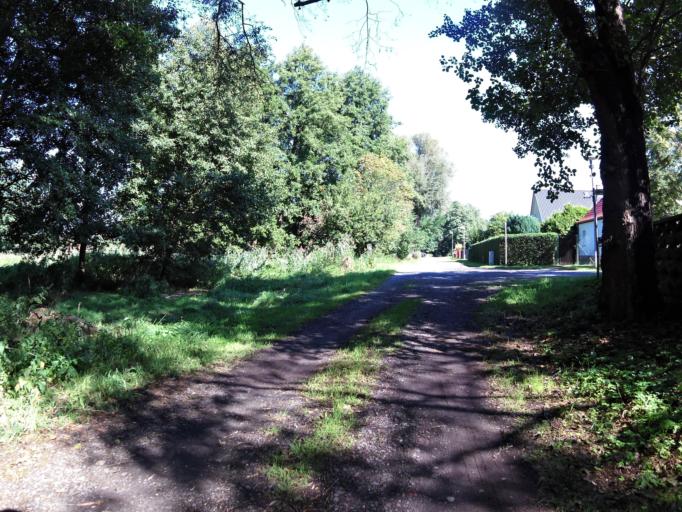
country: DE
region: Brandenburg
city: Storkow
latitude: 52.2493
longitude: 13.9387
